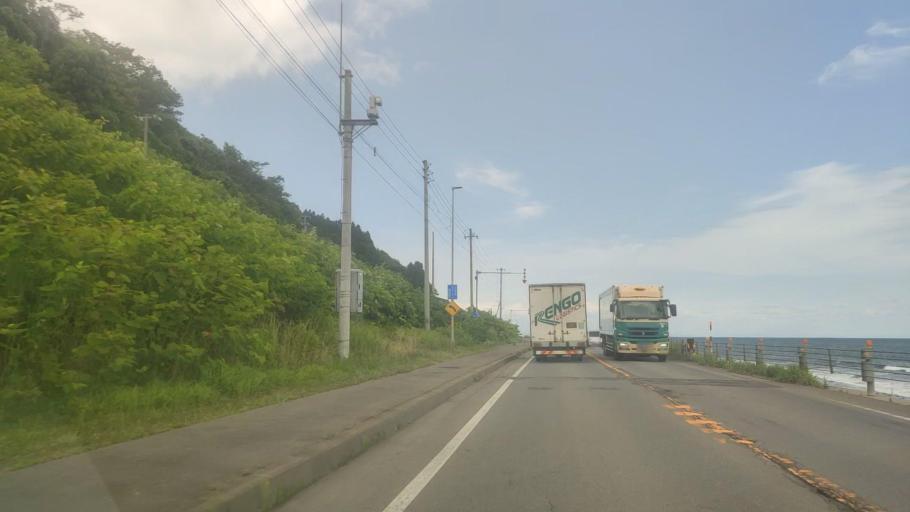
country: JP
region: Hokkaido
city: Nanae
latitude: 42.1450
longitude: 140.5002
